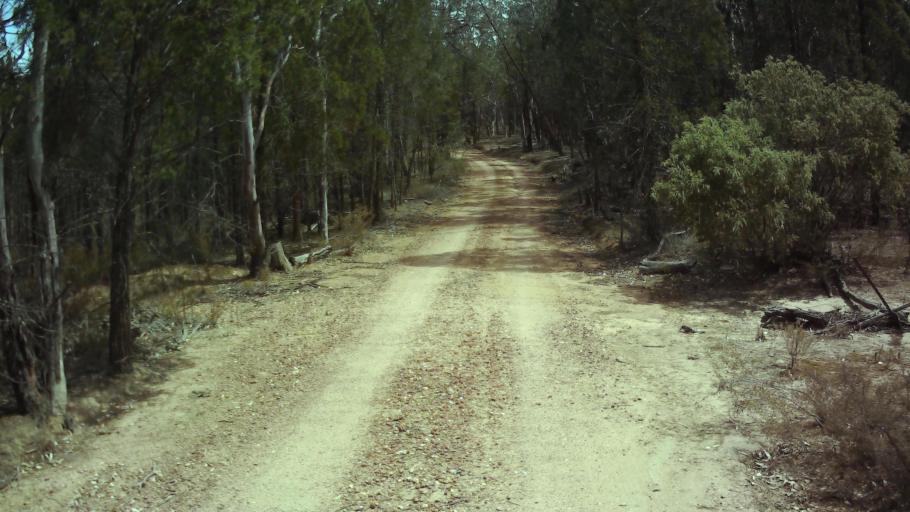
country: AU
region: New South Wales
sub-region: Weddin
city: Grenfell
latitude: -33.8917
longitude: 148.3883
